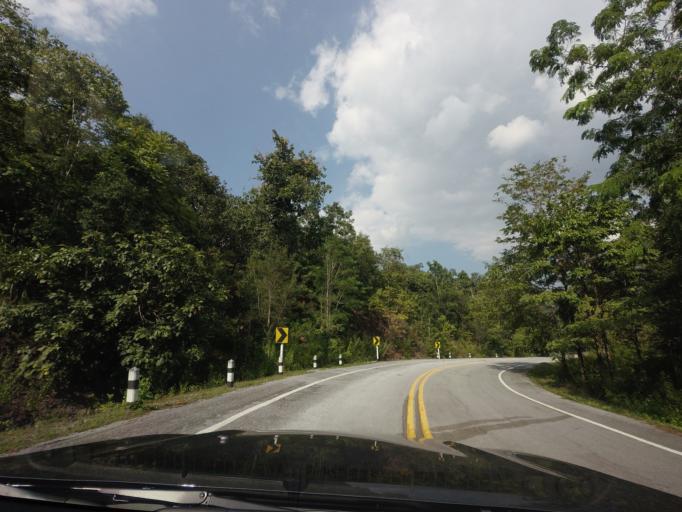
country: TH
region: Nan
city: Na Noi
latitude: 18.2765
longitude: 100.9686
